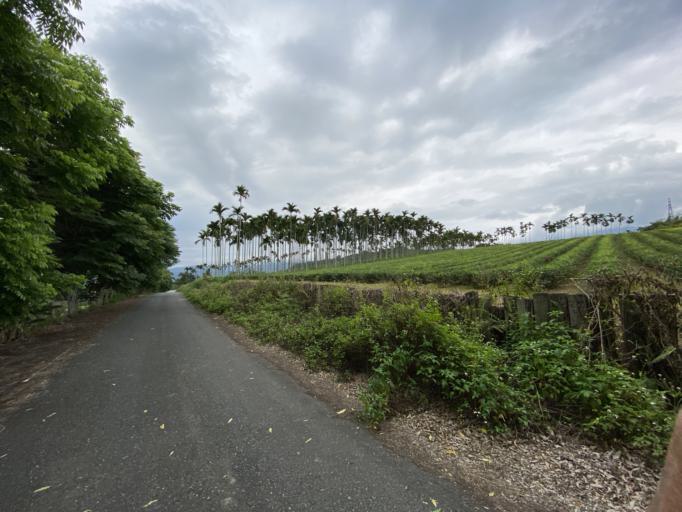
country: TW
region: Taiwan
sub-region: Hualien
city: Hualian
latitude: 23.4714
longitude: 121.3591
